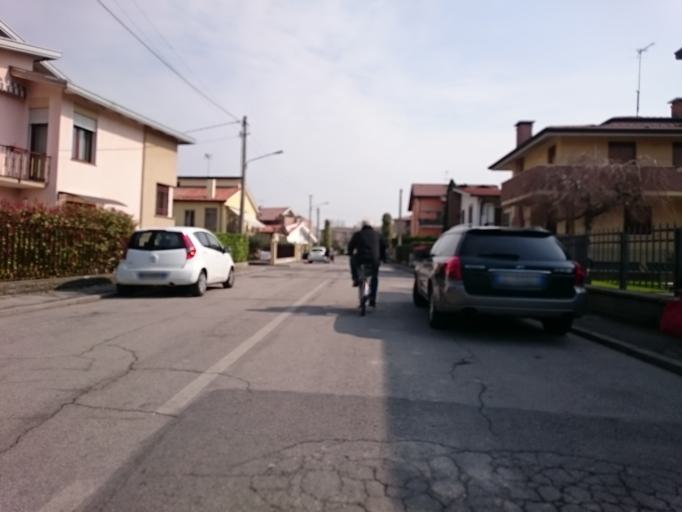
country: IT
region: Veneto
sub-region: Provincia di Padova
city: Padova
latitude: 45.3806
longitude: 11.8849
